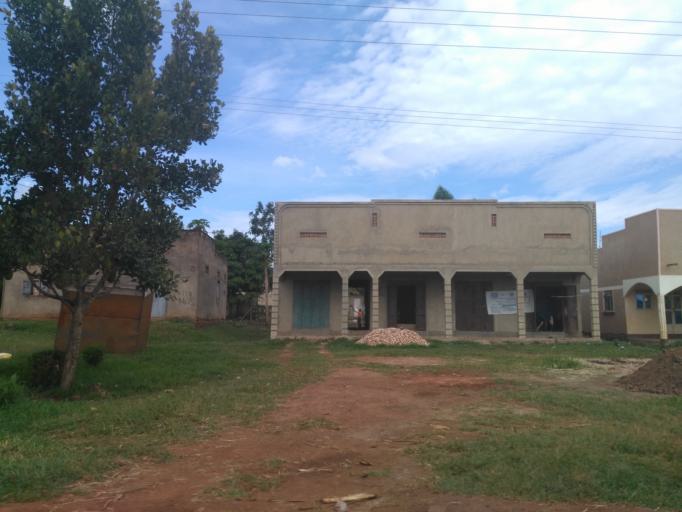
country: UG
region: Central Region
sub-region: Buikwe District
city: Njeru
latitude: 0.3992
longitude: 33.1753
